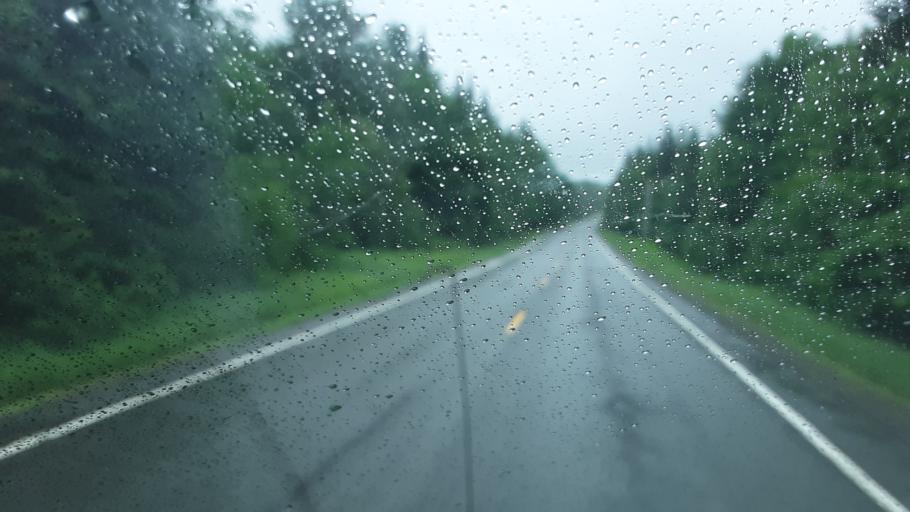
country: US
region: Maine
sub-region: Penobscot County
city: Patten
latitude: 46.1923
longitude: -68.3337
